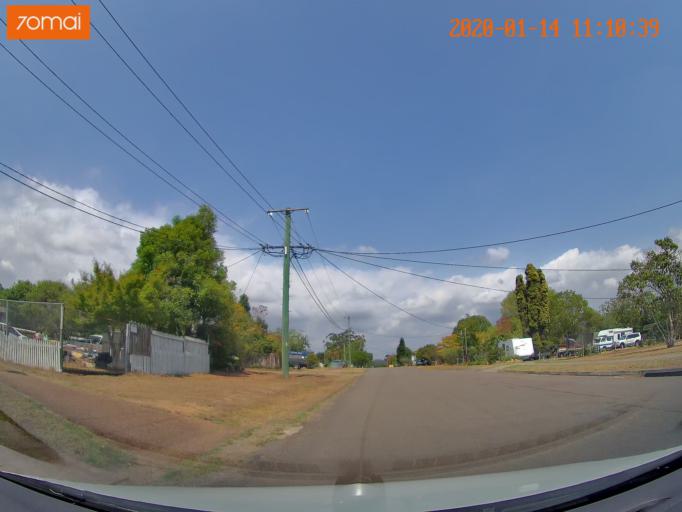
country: AU
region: New South Wales
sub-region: Lake Macquarie Shire
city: Dora Creek
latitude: -33.0960
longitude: 151.4767
